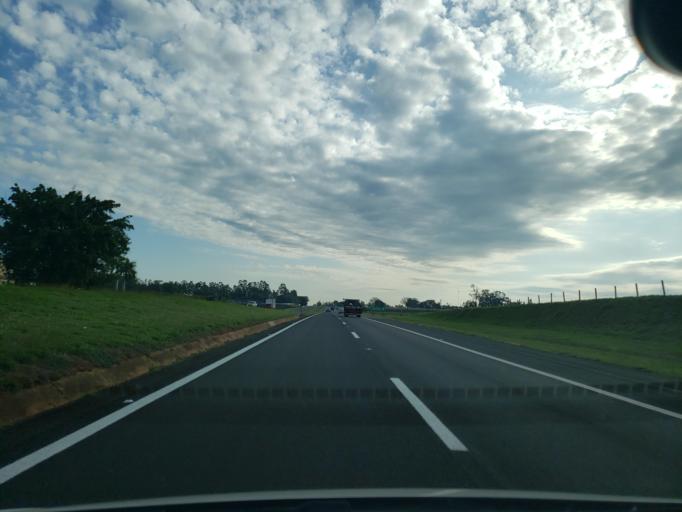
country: BR
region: Sao Paulo
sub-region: Guararapes
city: Guararapes
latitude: -21.2081
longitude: -50.6557
